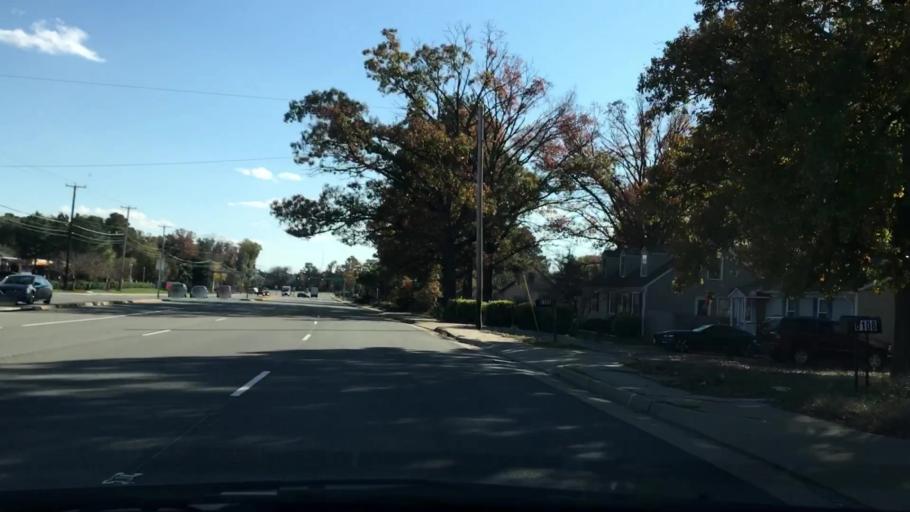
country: US
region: Virginia
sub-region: Henrico County
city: Dumbarton
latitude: 37.6093
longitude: -77.4962
